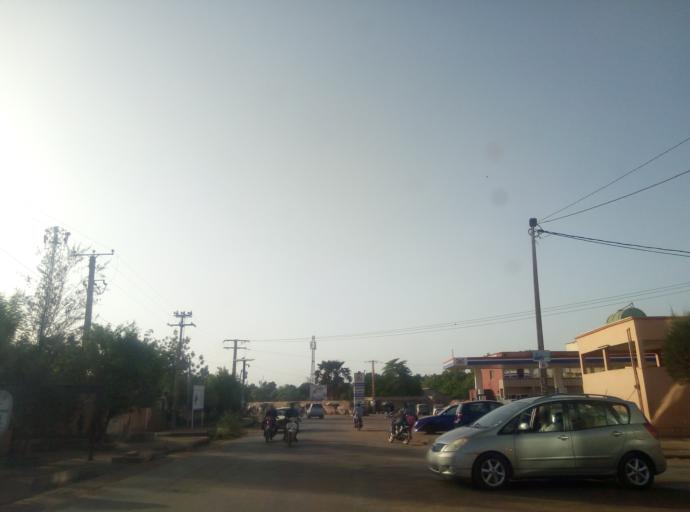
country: ML
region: Bamako
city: Bamako
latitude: 12.6100
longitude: -7.9729
